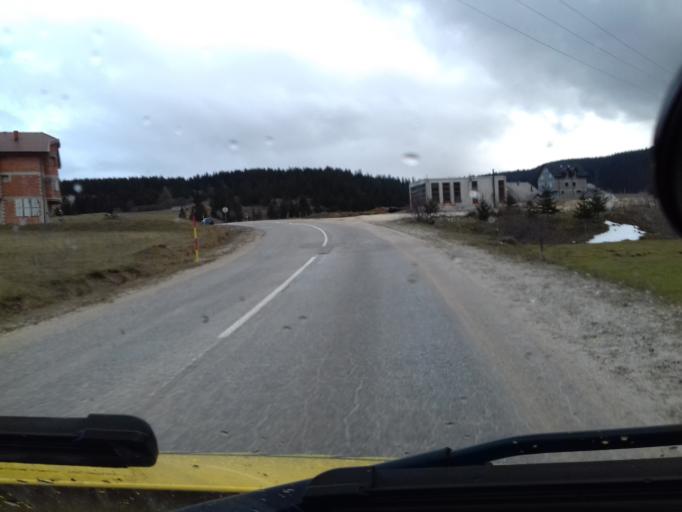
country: BA
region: Federation of Bosnia and Herzegovina
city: Turbe
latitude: 44.3081
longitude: 17.5456
